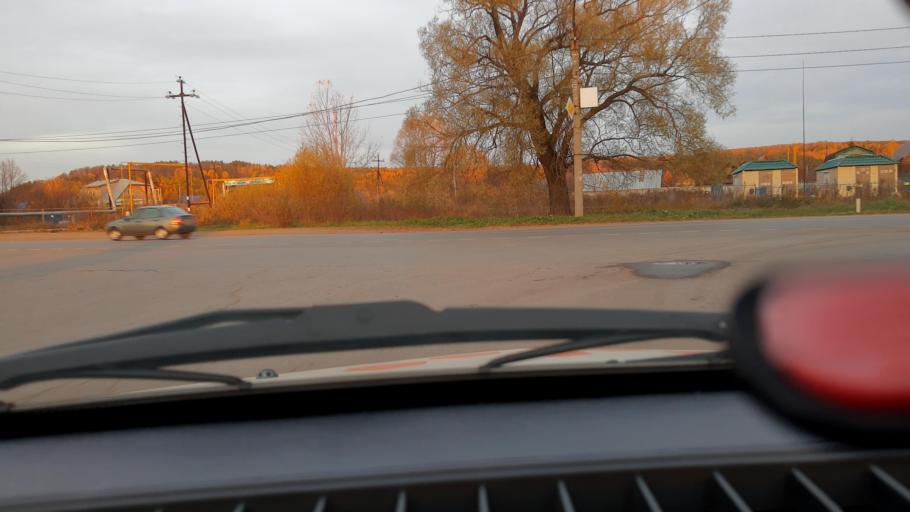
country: RU
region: Bashkortostan
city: Ufa
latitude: 54.8110
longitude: 56.1608
